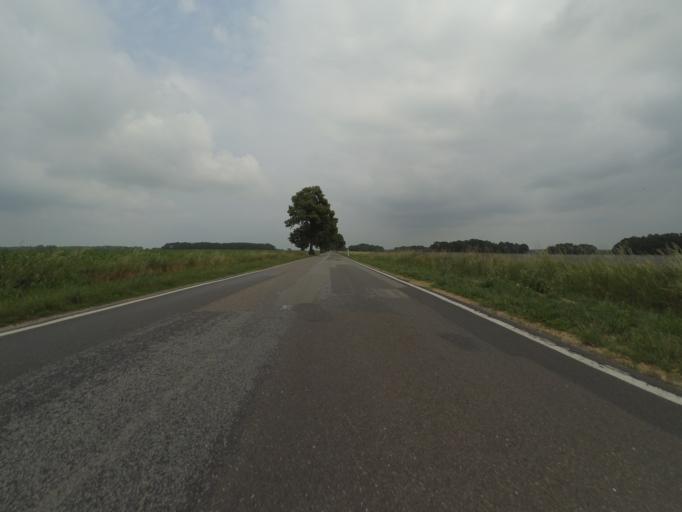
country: DE
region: Mecklenburg-Vorpommern
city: Siggelkow
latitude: 53.3852
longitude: 11.9588
